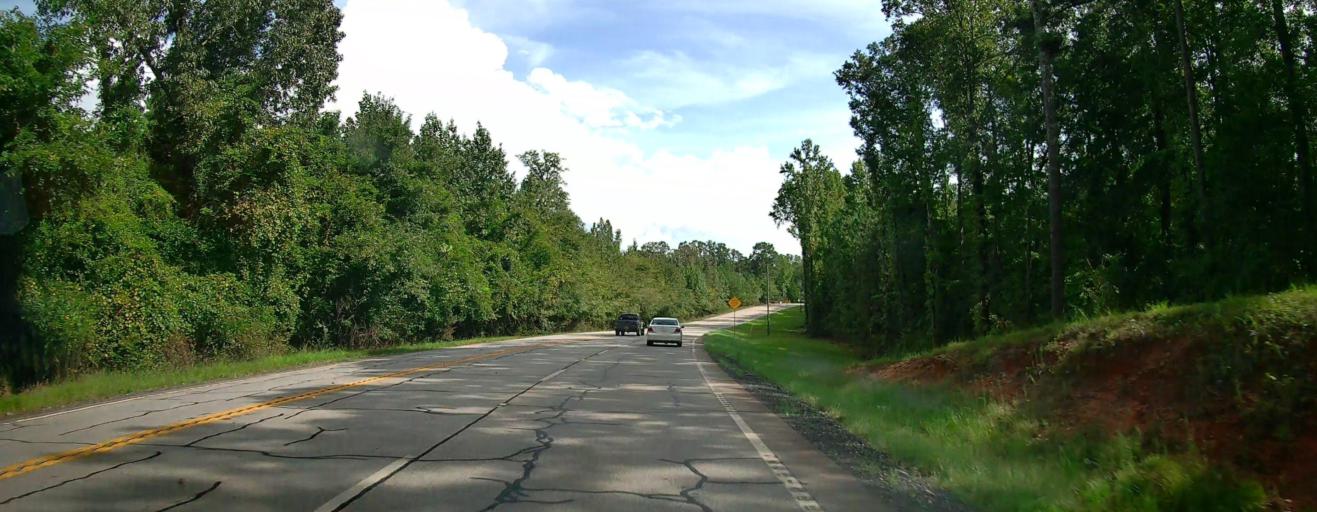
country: US
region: Georgia
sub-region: Harris County
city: Hamilton
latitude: 32.7003
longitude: -84.8578
